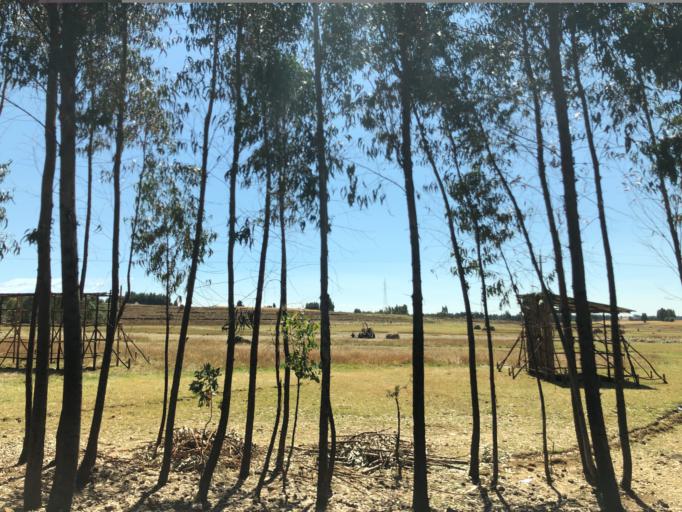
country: ET
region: Amhara
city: Lalibela
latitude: 11.6786
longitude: 38.8997
